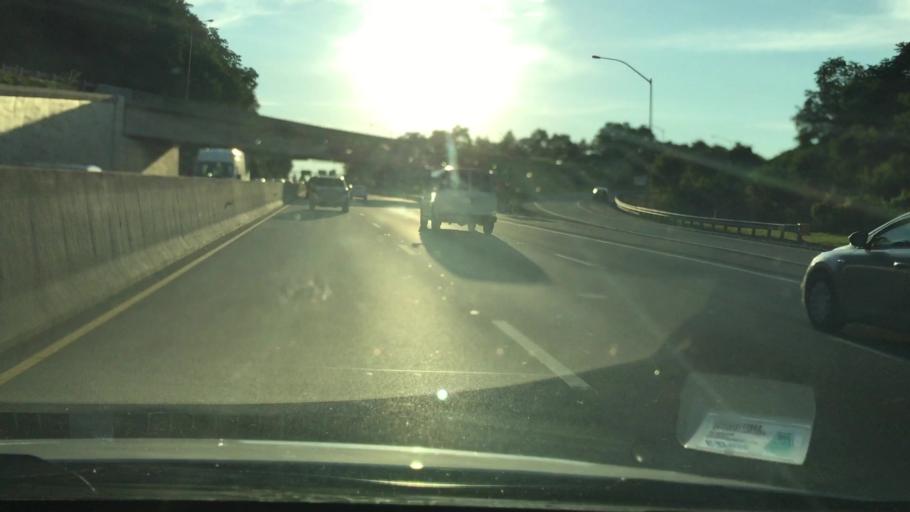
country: US
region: Pennsylvania
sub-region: Allegheny County
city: Green Tree
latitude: 40.4199
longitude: -80.0364
